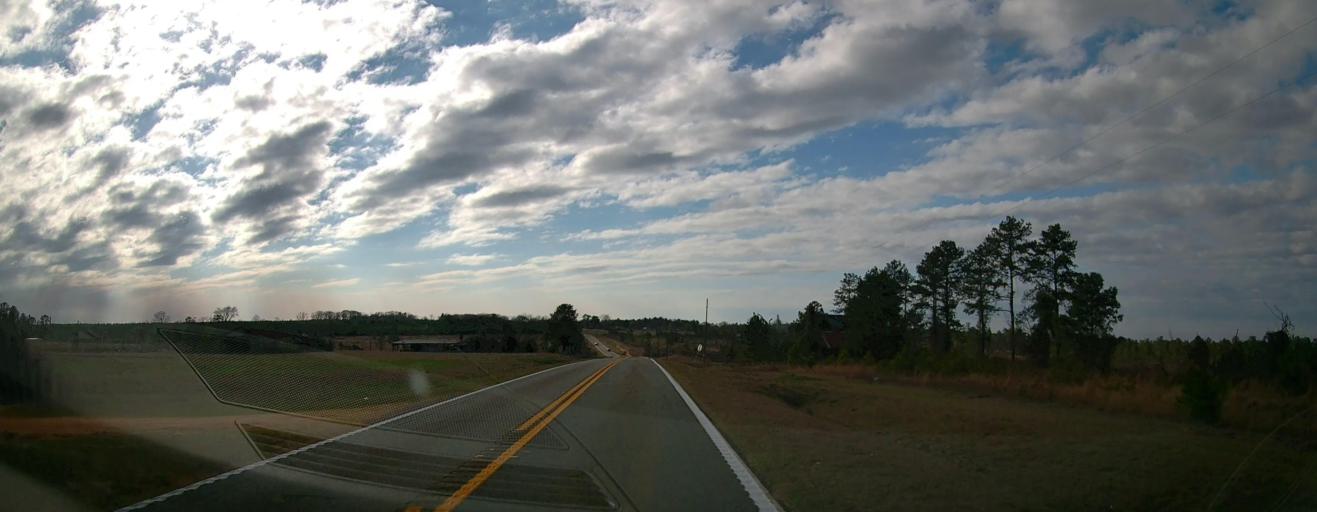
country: US
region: Georgia
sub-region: Marion County
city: Buena Vista
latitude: 32.4446
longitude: -84.5237
